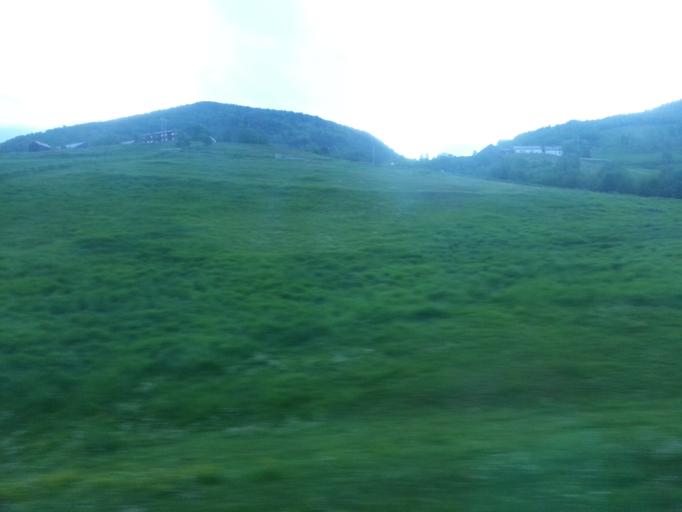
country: NO
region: Oppland
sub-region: Dovre
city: Dovre
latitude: 62.0002
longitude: 9.2387
